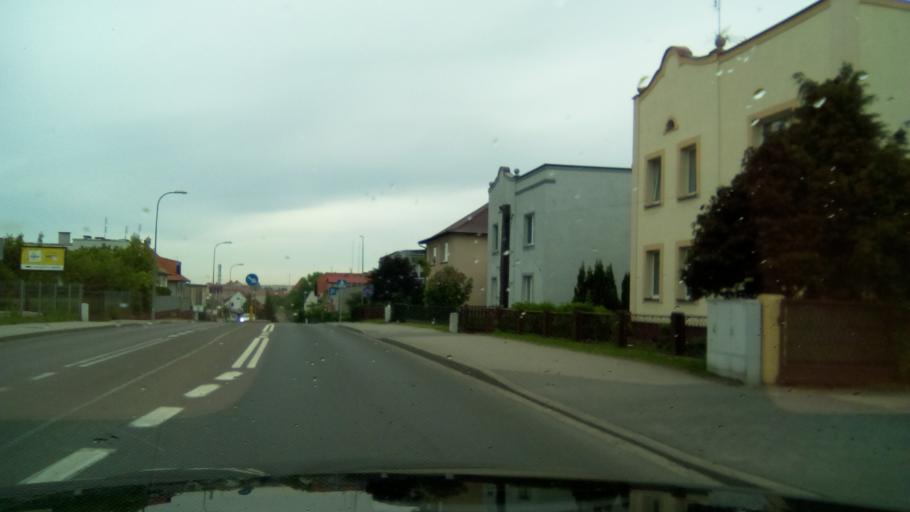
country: PL
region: Pomeranian Voivodeship
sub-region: Powiat chojnicki
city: Chojnice
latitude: 53.6908
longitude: 17.5528
